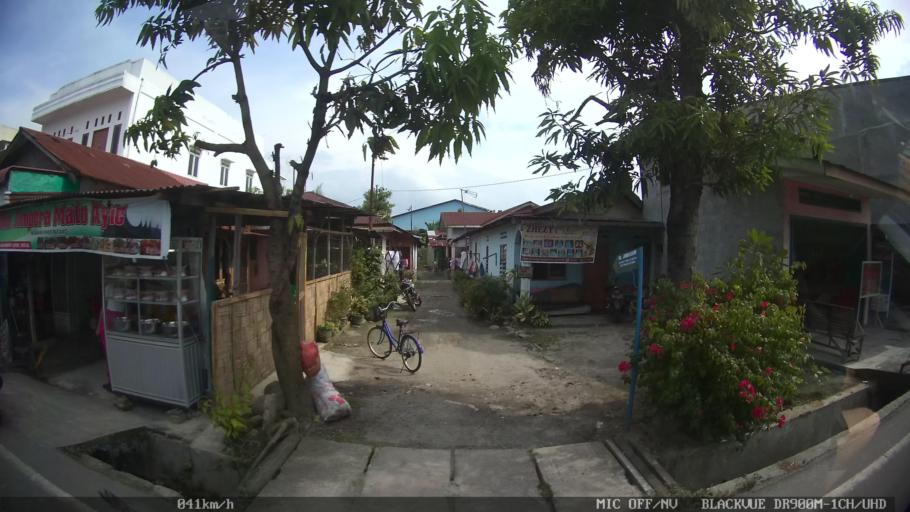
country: ID
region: North Sumatra
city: Percut
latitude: 3.6071
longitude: 98.7714
